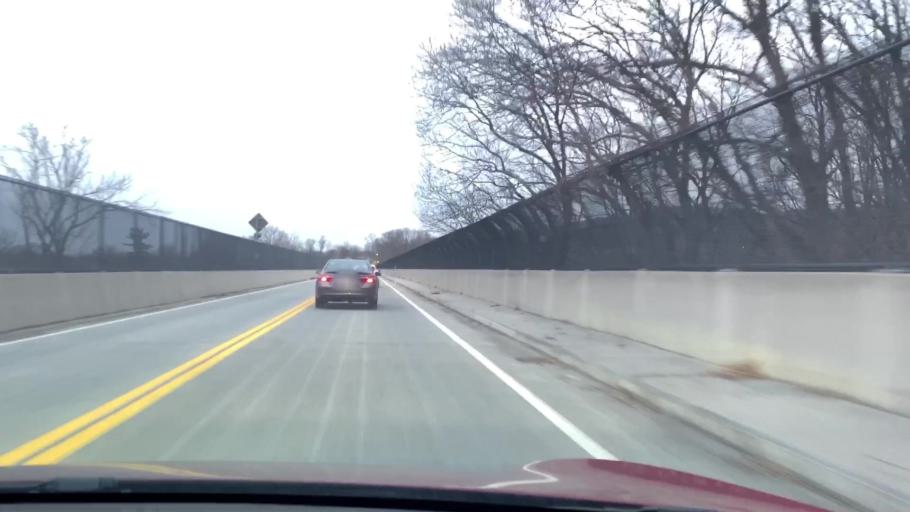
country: US
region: New York
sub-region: Rockland County
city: Sparkill
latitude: 41.0293
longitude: -73.9242
